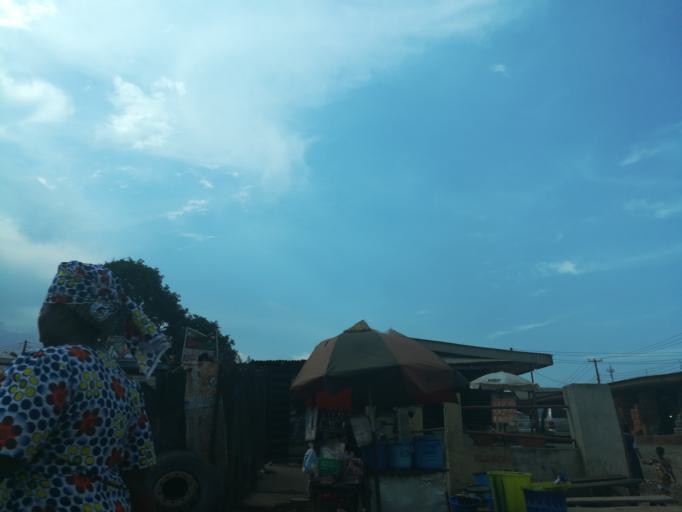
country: NG
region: Lagos
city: Ikorodu
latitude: 6.6278
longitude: 3.5084
